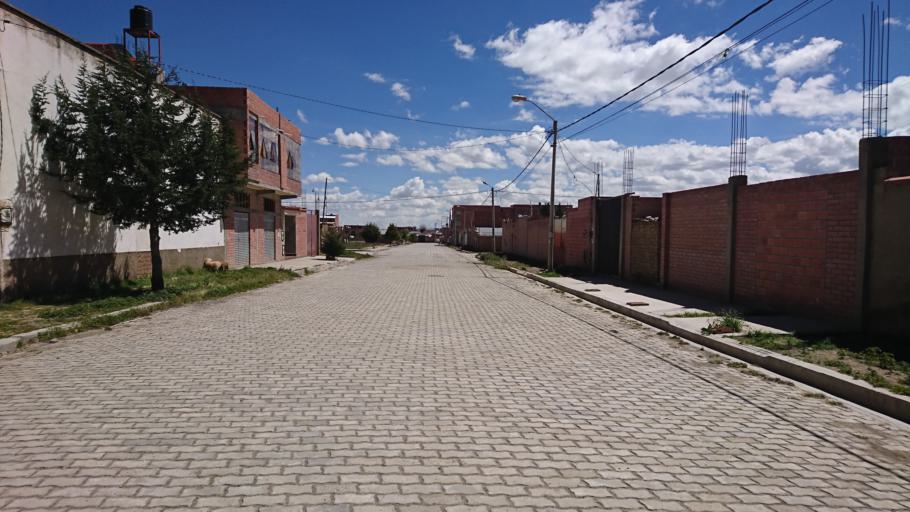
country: BO
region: La Paz
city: La Paz
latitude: -16.5012
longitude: -68.1873
